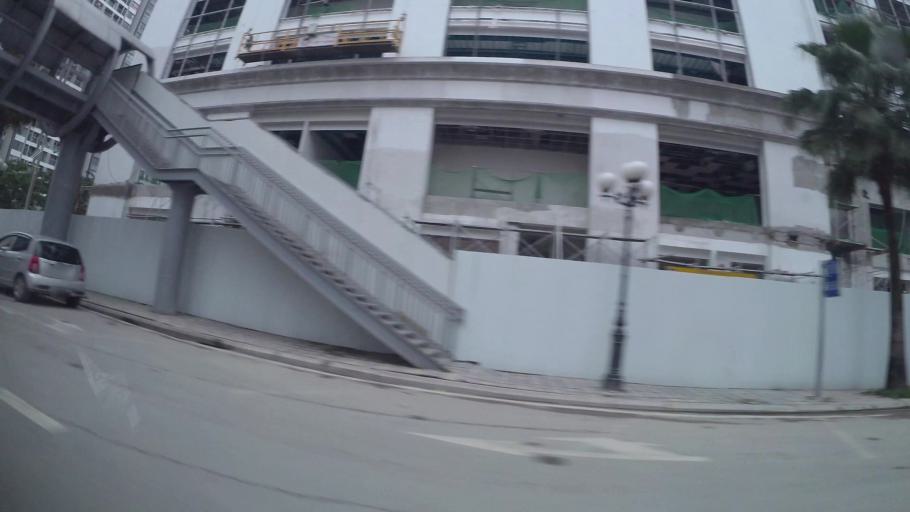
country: VN
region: Ha Noi
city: Hai BaTrung
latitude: 20.9936
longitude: 105.8675
